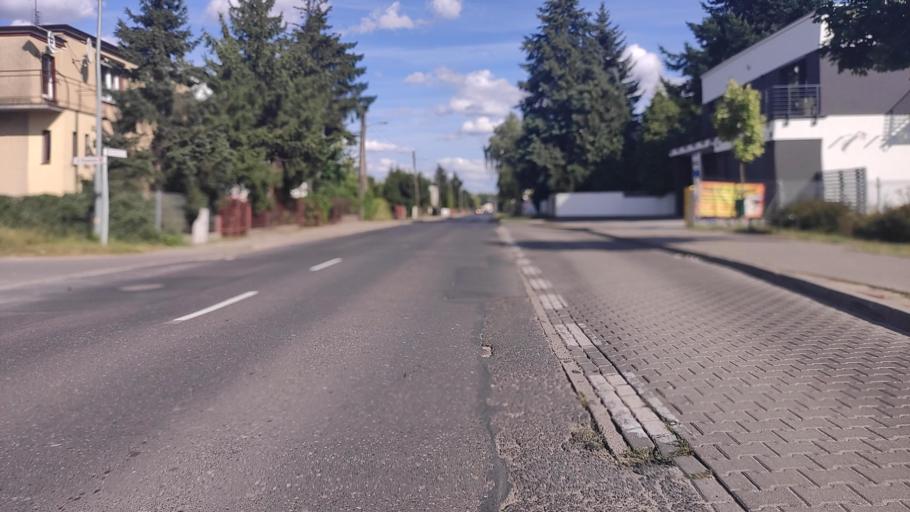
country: PL
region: Greater Poland Voivodeship
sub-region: Powiat poznanski
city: Swarzedz
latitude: 52.3977
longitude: 17.0722
